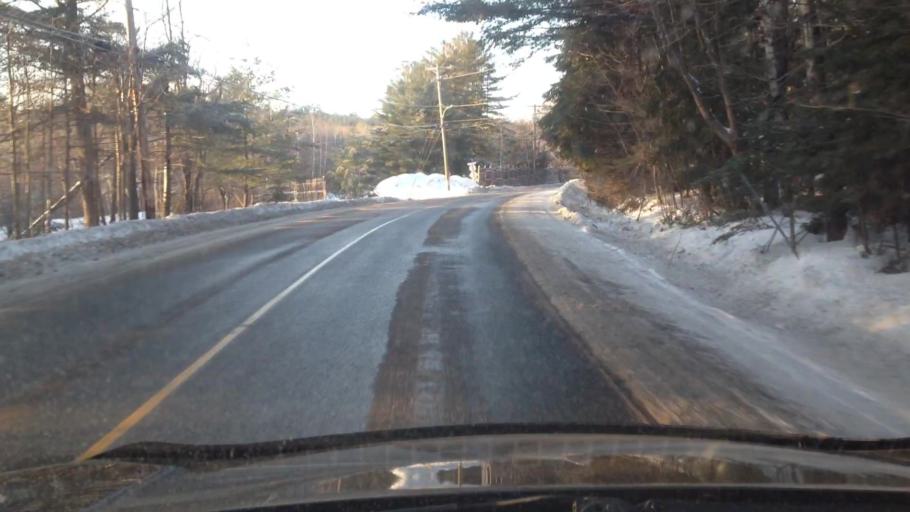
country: CA
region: Quebec
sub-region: Lanaudiere
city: Sainte-Julienne
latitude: 45.9532
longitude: -73.7538
